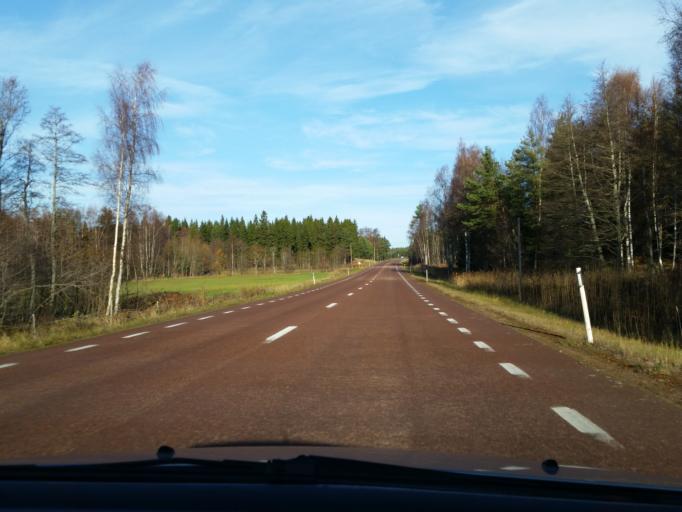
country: AX
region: Alands landsbygd
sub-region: Finstroem
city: Finstroem
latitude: 60.2977
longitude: 19.9529
